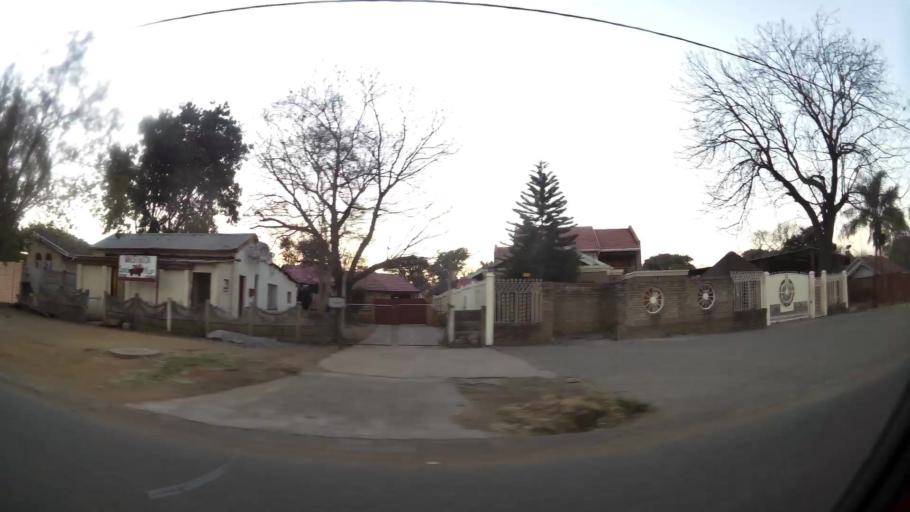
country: ZA
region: North-West
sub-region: Bojanala Platinum District Municipality
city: Rustenburg
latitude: -25.6595
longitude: 27.2356
